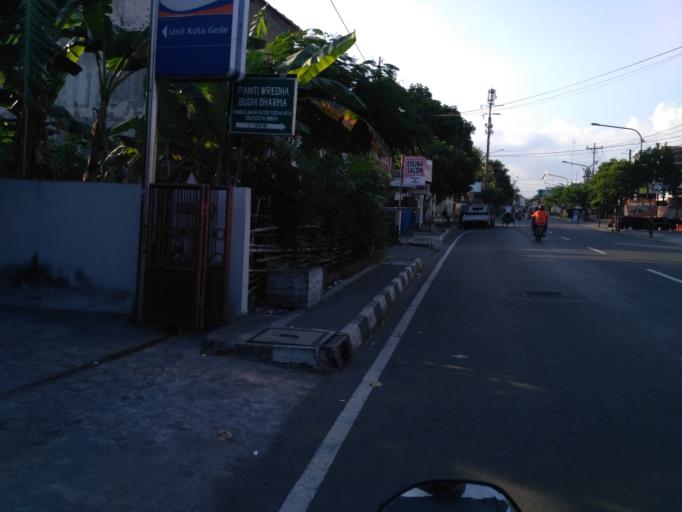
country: ID
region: Daerah Istimewa Yogyakarta
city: Yogyakarta
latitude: -7.8281
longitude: 110.3900
